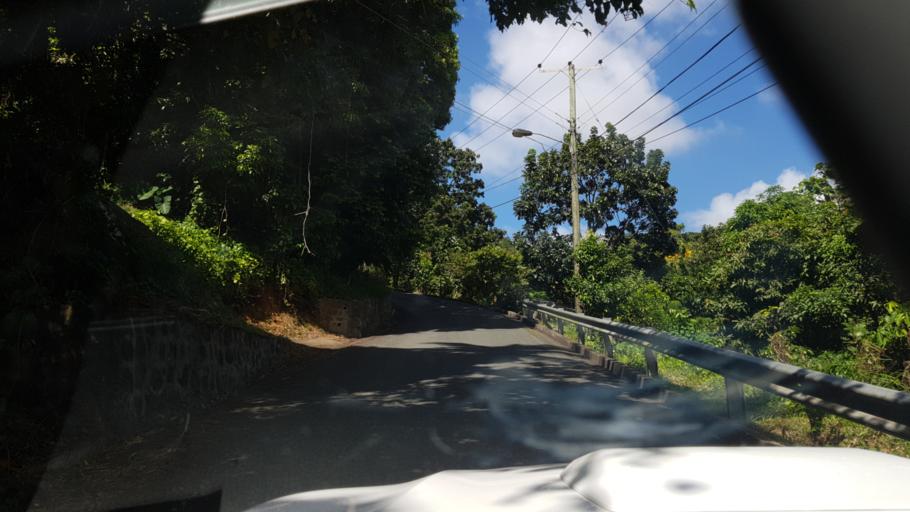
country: LC
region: Castries Quarter
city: Castries
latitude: 13.9814
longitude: -60.9737
